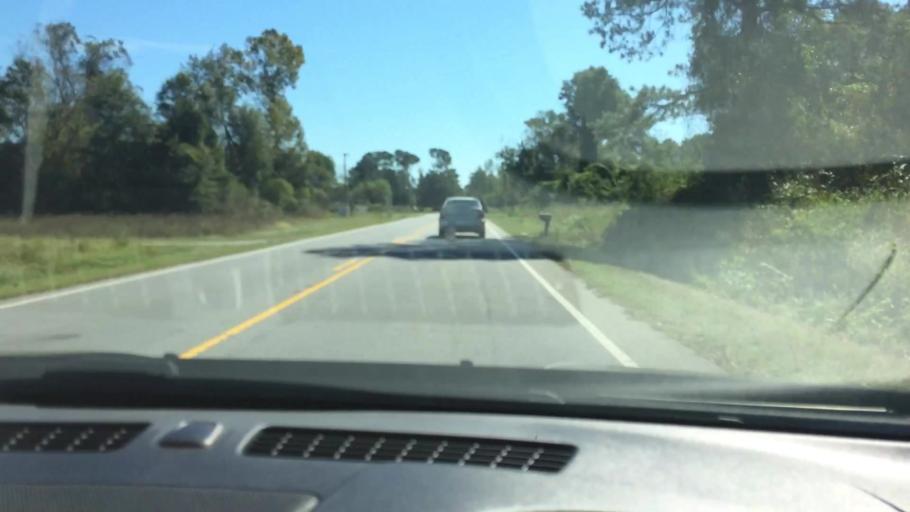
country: US
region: North Carolina
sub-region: Pitt County
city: Grifton
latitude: 35.3474
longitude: -77.3231
